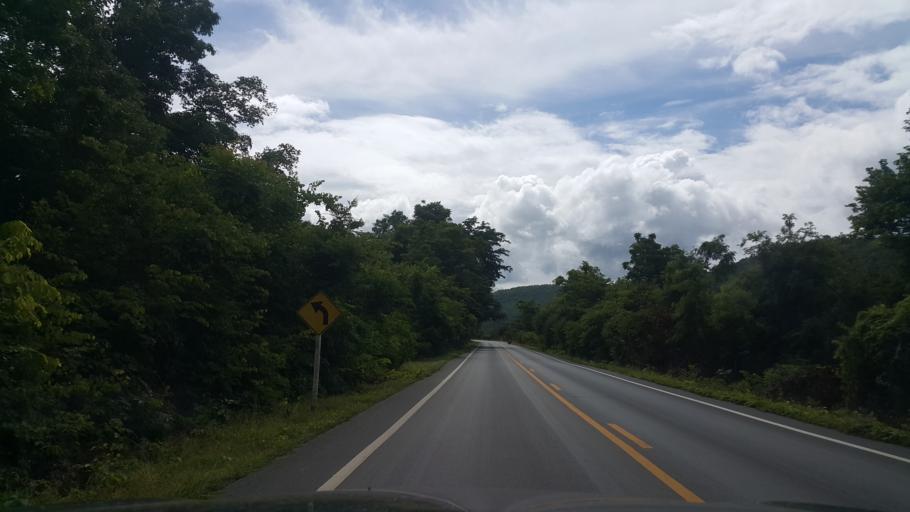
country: TH
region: Uttaradit
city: Thong Saen Khan
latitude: 17.3798
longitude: 100.2784
